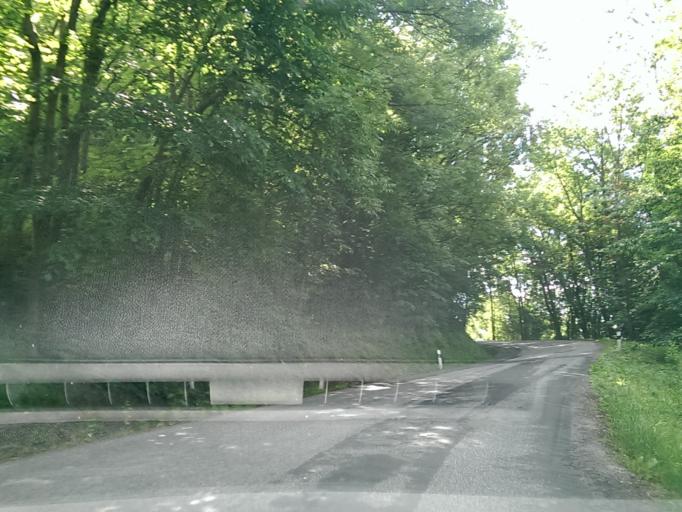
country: CZ
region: Liberecky
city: Rovensko pod Troskami
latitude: 50.5859
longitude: 15.2693
